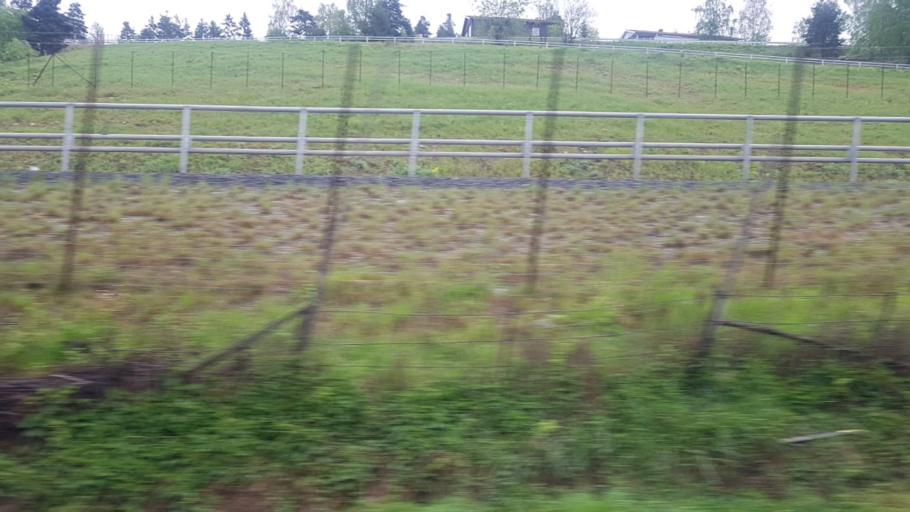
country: NO
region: Oppland
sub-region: Sor-Fron
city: Hundorp
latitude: 61.5633
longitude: 9.9157
